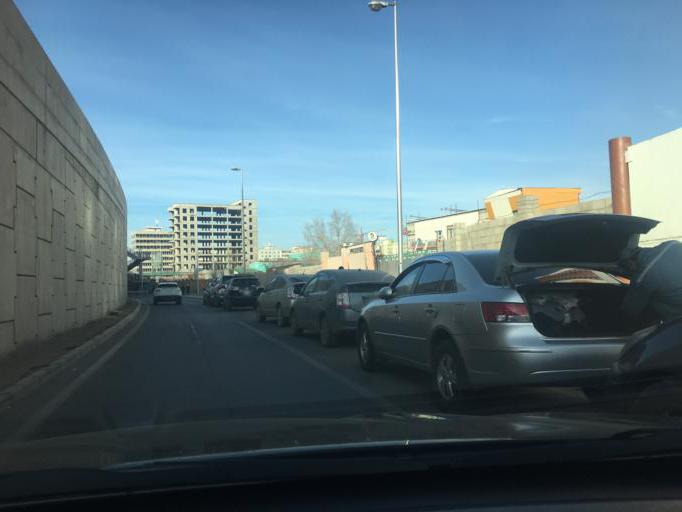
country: MN
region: Ulaanbaatar
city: Ulaanbaatar
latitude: 47.9060
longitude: 106.8945
